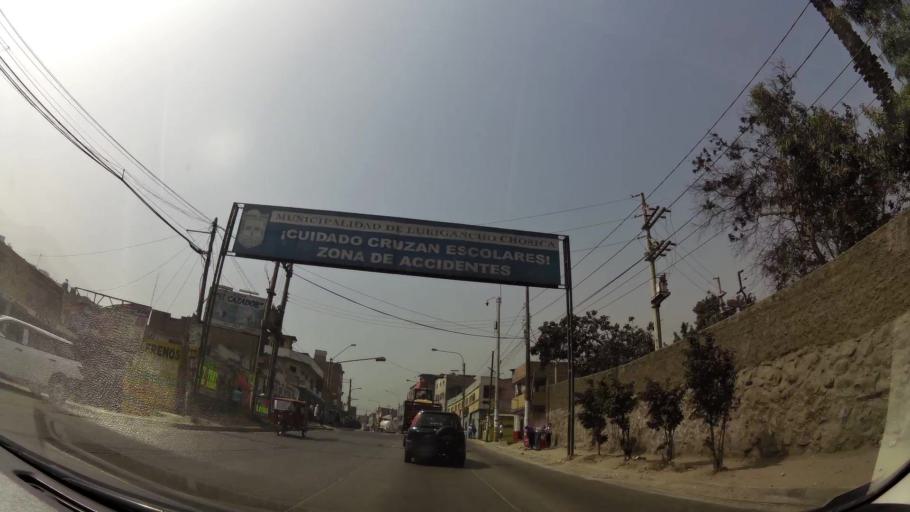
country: PE
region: Lima
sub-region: Lima
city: Chosica
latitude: -11.9426
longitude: -76.7041
